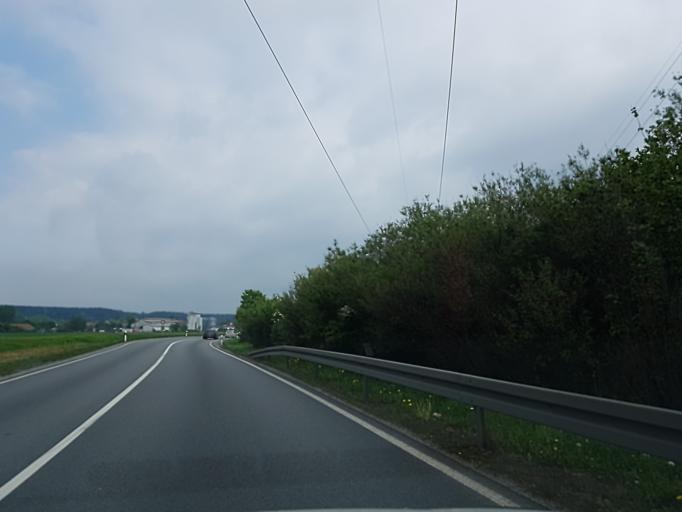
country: DE
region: Bavaria
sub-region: Upper Bavaria
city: Hohenlinden
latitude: 48.1486
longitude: 12.0018
